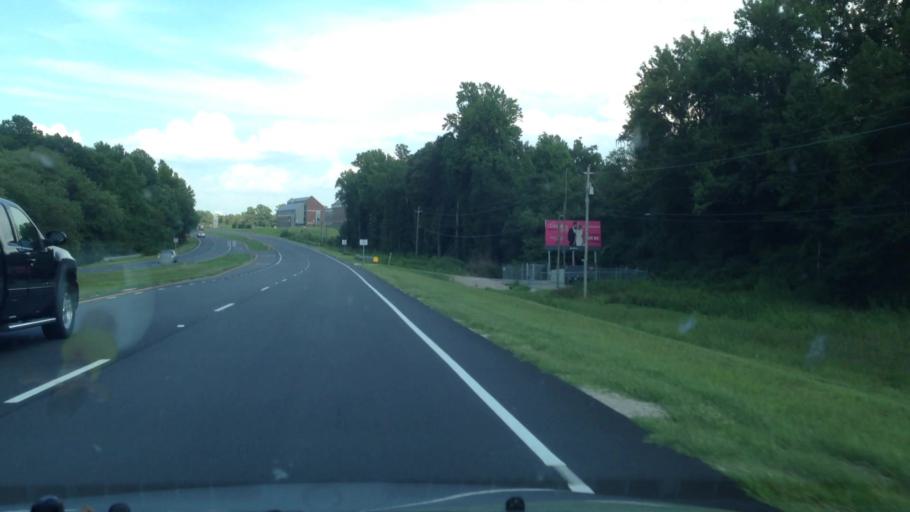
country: US
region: North Carolina
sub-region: Harnett County
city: Buies Creek
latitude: 35.4073
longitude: -78.7645
